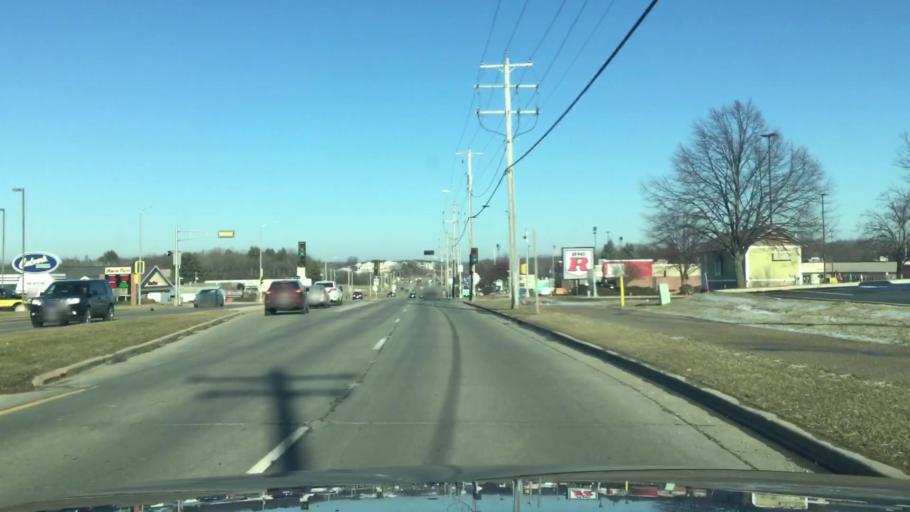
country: US
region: Wisconsin
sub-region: Racine County
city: Burlington
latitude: 42.6915
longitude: -88.2662
